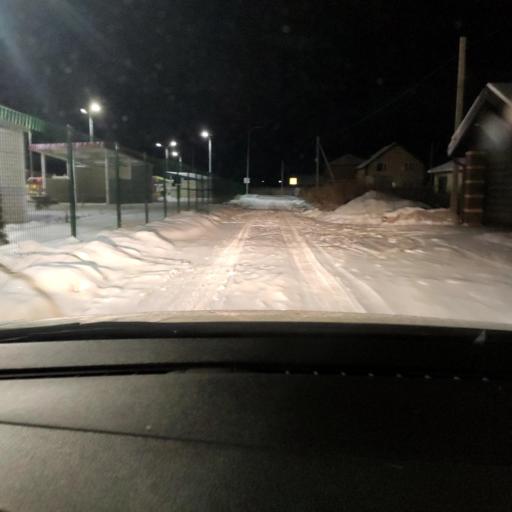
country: RU
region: Tatarstan
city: Stolbishchi
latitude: 55.6848
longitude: 49.2215
